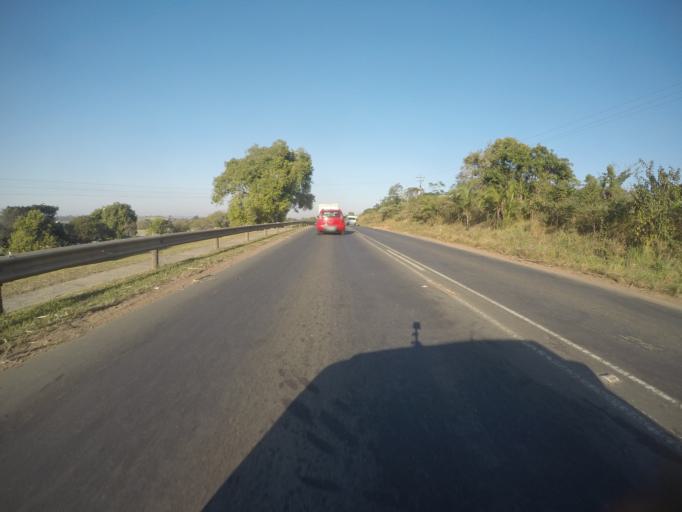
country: ZA
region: KwaZulu-Natal
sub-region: iLembe District Municipality
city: Stanger
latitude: -29.4055
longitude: 31.2491
